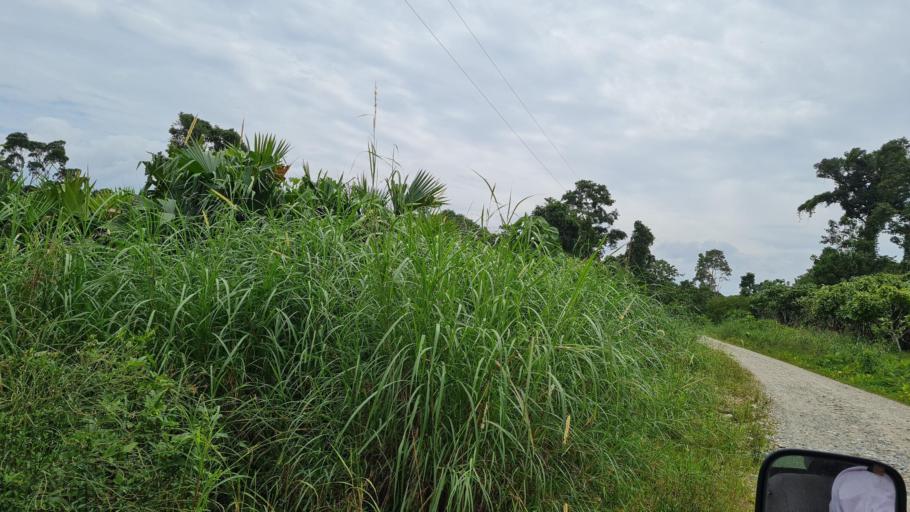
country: EC
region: Napo
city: Tena
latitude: -0.9946
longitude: -77.7524
